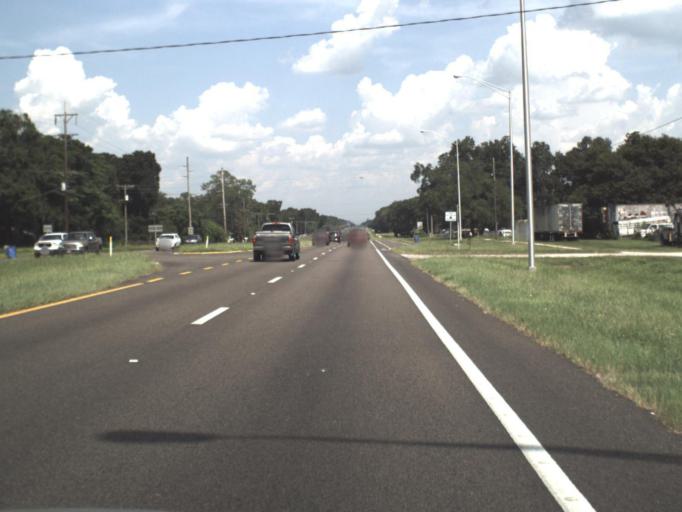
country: US
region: Florida
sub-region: Hillsborough County
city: Valrico
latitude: 27.9375
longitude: -82.1689
